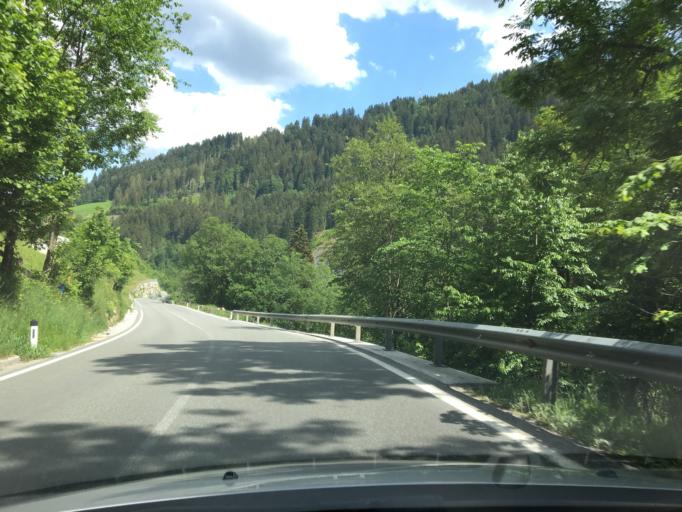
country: AT
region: Salzburg
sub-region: Politischer Bezirk Sankt Johann im Pongau
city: Sankt Johann im Pongau
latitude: 47.3312
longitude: 13.2286
